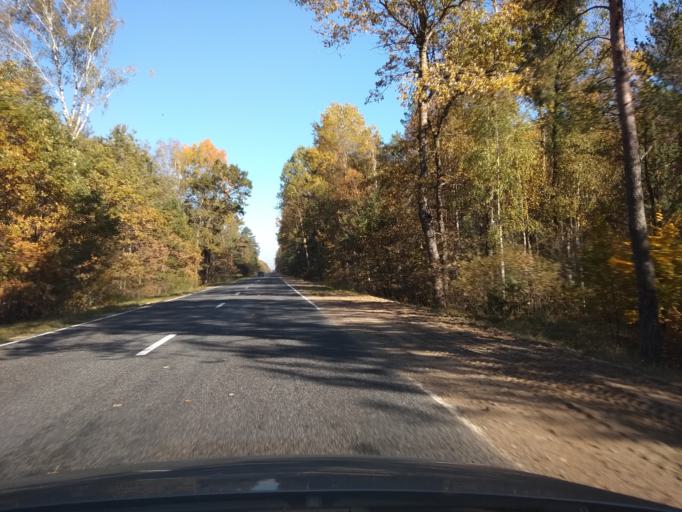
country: BY
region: Brest
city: Malaryta
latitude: 51.9240
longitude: 24.1627
